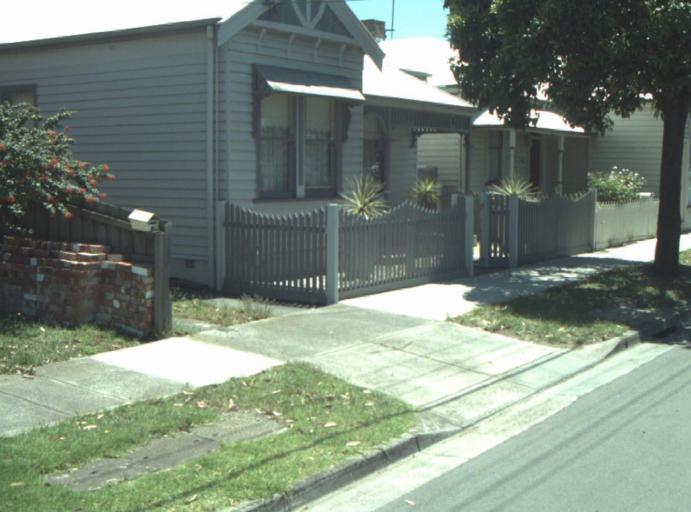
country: AU
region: Victoria
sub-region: Greater Geelong
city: Geelong
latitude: -38.1579
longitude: 144.3506
